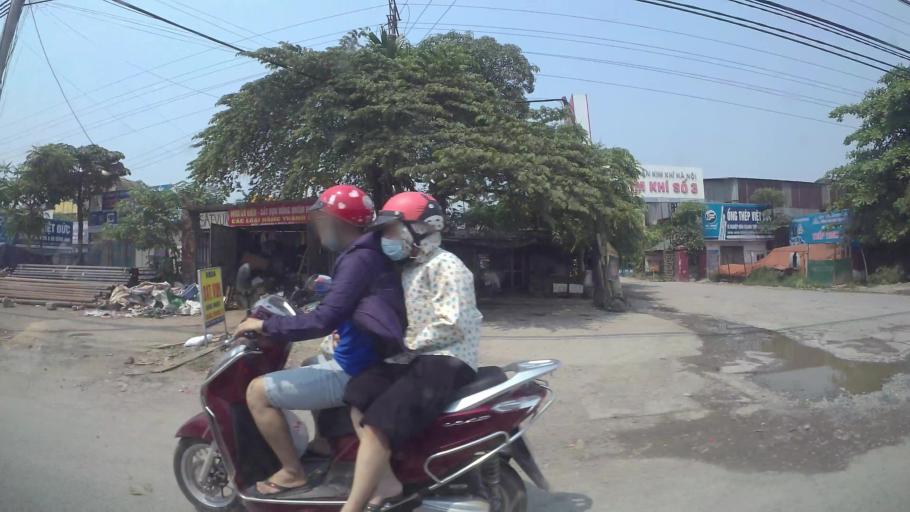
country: VN
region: Ha Noi
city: Van Dien
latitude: 20.9480
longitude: 105.8254
